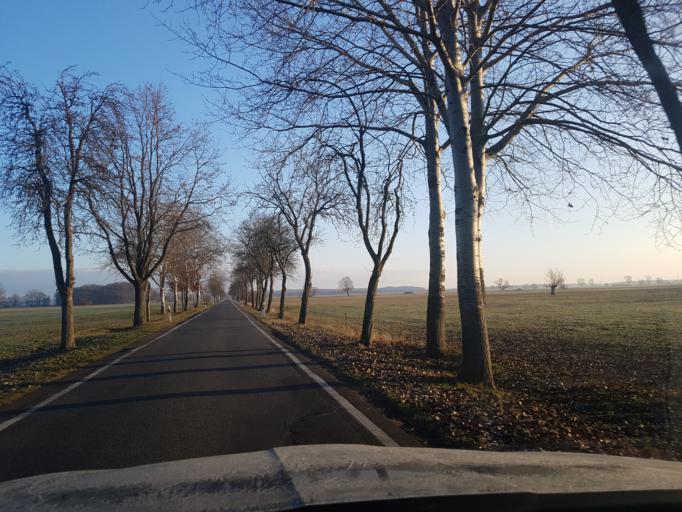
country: DE
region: Brandenburg
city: Schlieben
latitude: 51.7004
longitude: 13.3376
